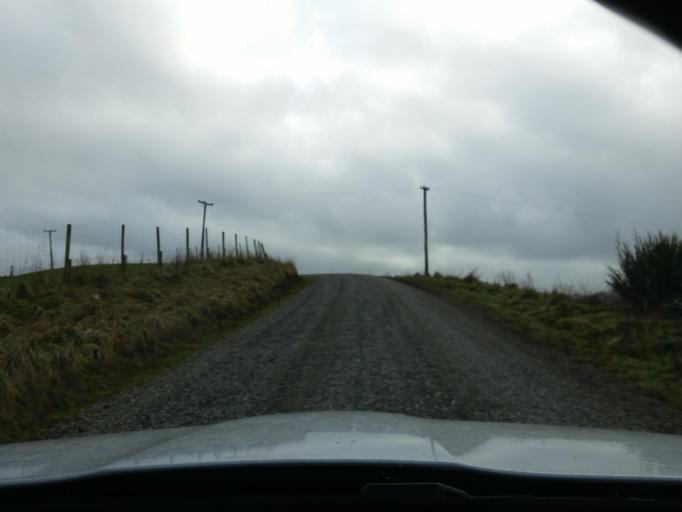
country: NZ
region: Southland
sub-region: Southland District
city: Riverton
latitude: -46.0659
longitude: 167.7800
